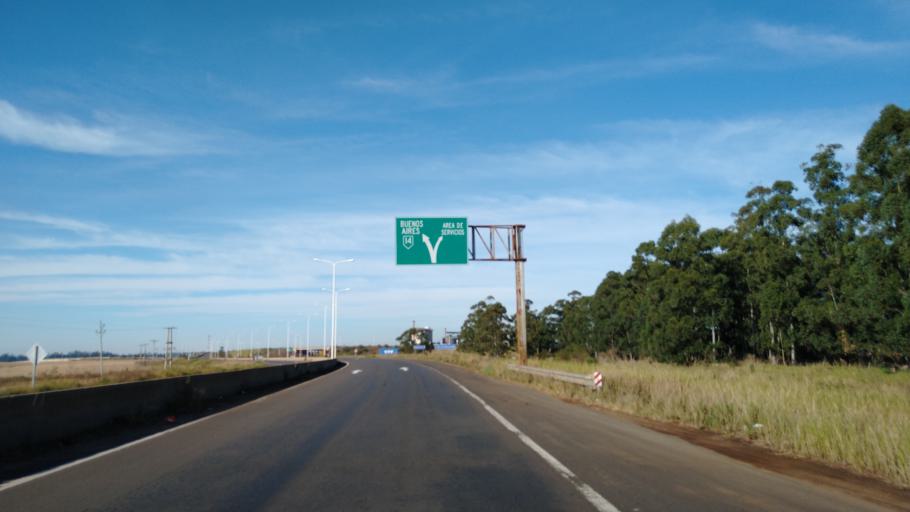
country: AR
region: Corrientes
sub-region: Departamento de Paso de los Libres
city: Paso de los Libres
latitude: -29.7061
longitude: -57.2104
